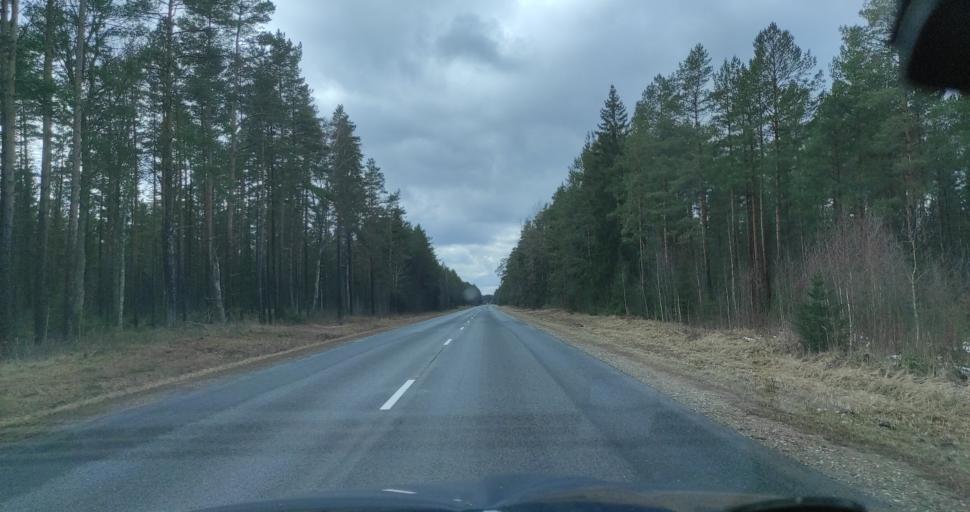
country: LV
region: Talsu Rajons
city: Stende
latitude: 57.1138
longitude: 22.5074
